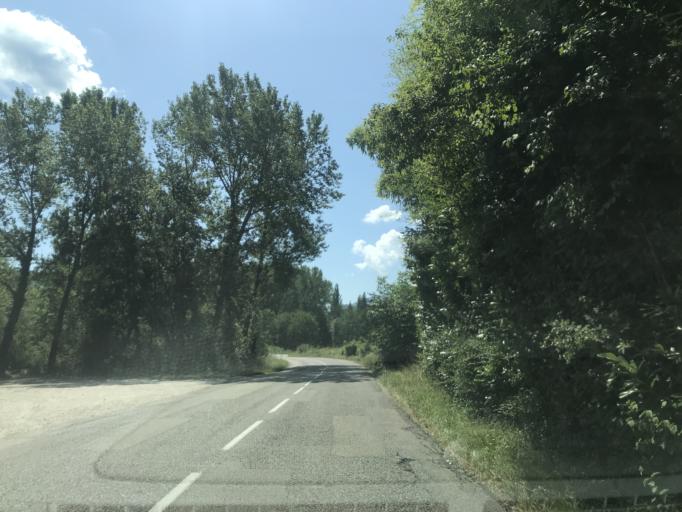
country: FR
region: Rhone-Alpes
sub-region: Departement de la Savoie
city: Chatillon
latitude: 45.8146
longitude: 5.8140
